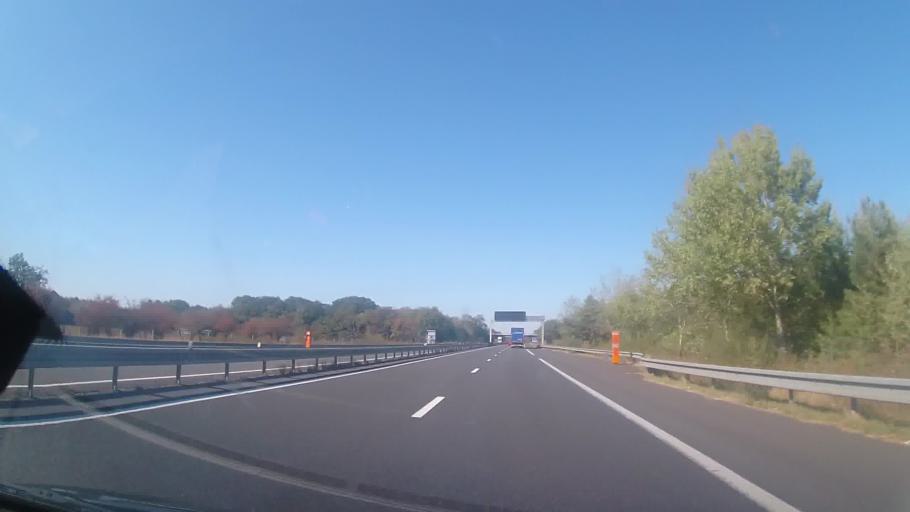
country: FR
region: Centre
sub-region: Departement du Loiret
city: Jouy-le-Potier
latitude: 47.7640
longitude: 1.8527
